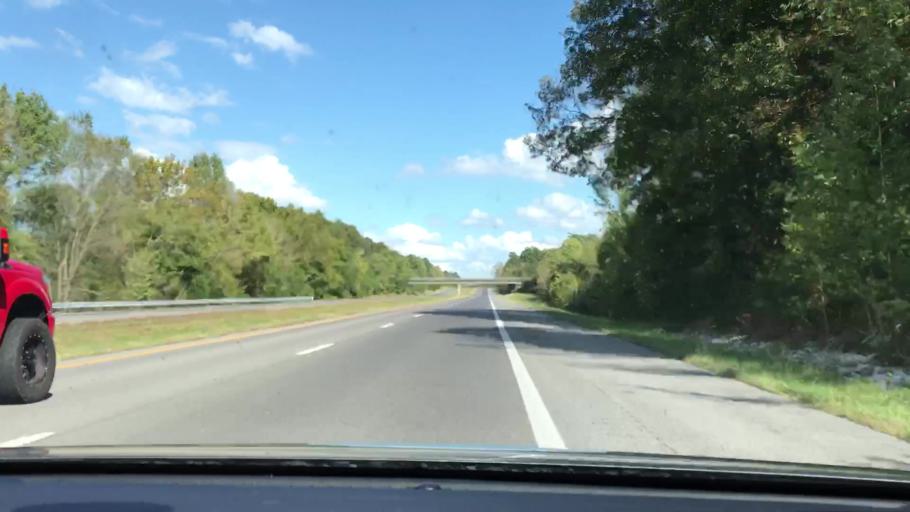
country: US
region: Kentucky
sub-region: Marshall County
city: Benton
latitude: 36.8353
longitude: -88.4331
